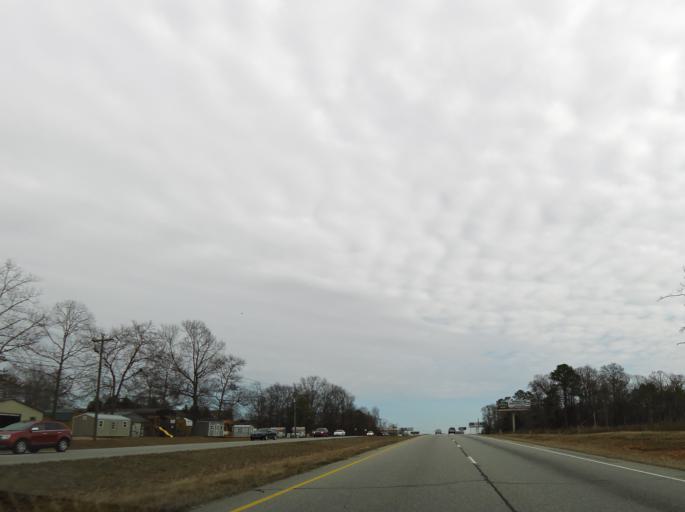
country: US
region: Georgia
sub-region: Houston County
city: Centerville
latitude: 32.6150
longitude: -83.7330
